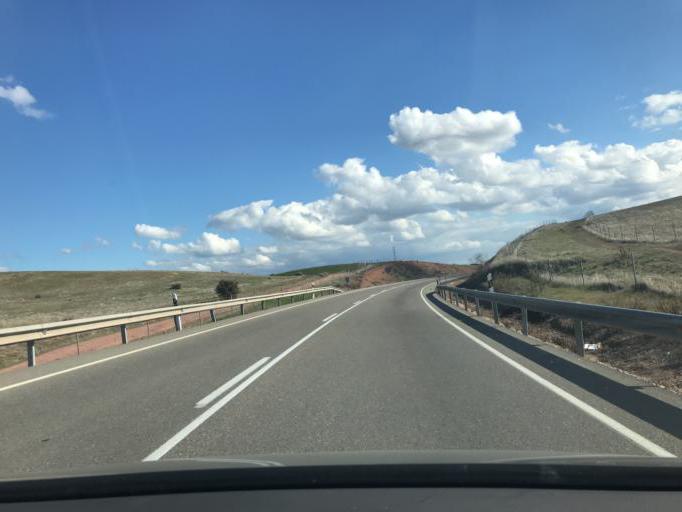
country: ES
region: Andalusia
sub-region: Province of Cordoba
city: Penarroya-Pueblonuevo
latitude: 38.3060
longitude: -5.2589
